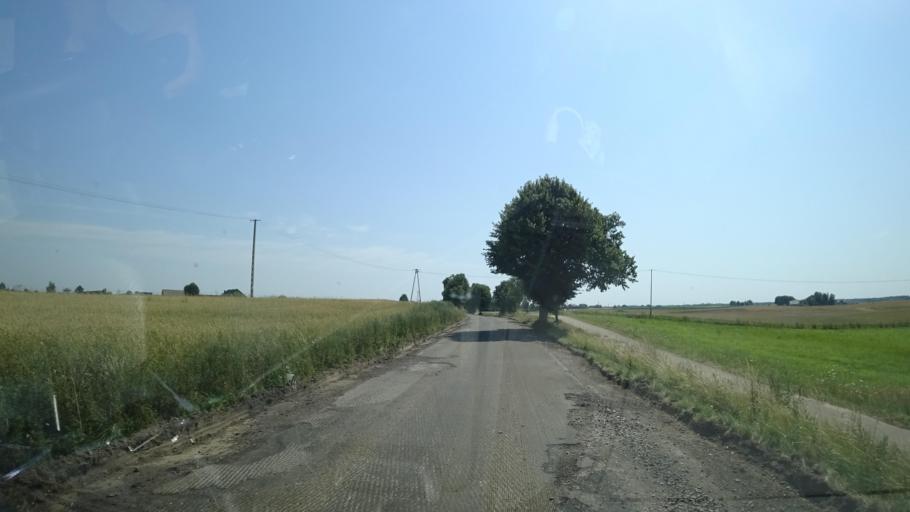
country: PL
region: Pomeranian Voivodeship
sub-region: Powiat chojnicki
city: Brusy
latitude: 53.8730
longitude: 17.6634
